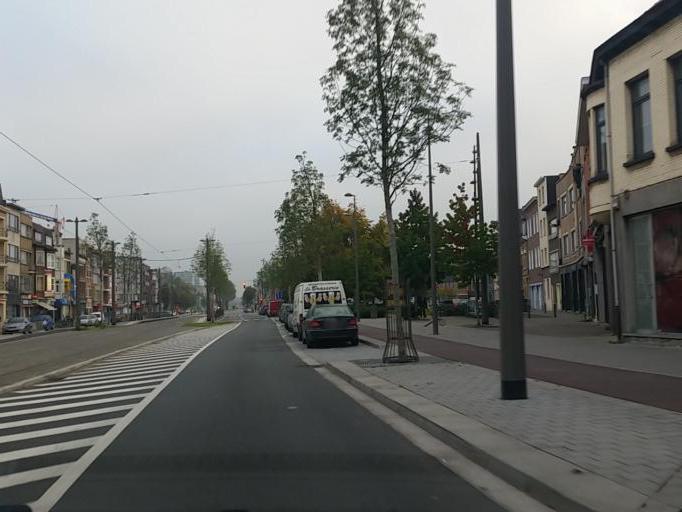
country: BE
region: Flanders
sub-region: Provincie Antwerpen
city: Schoten
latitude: 51.2482
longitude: 4.4536
